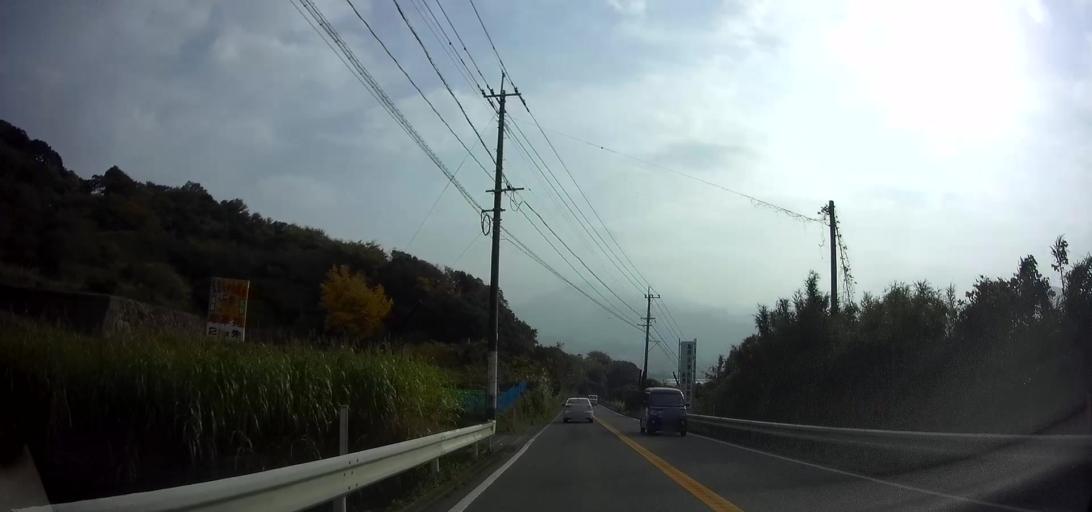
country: JP
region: Nagasaki
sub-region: Isahaya-shi
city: Isahaya
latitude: 32.7951
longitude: 130.1810
